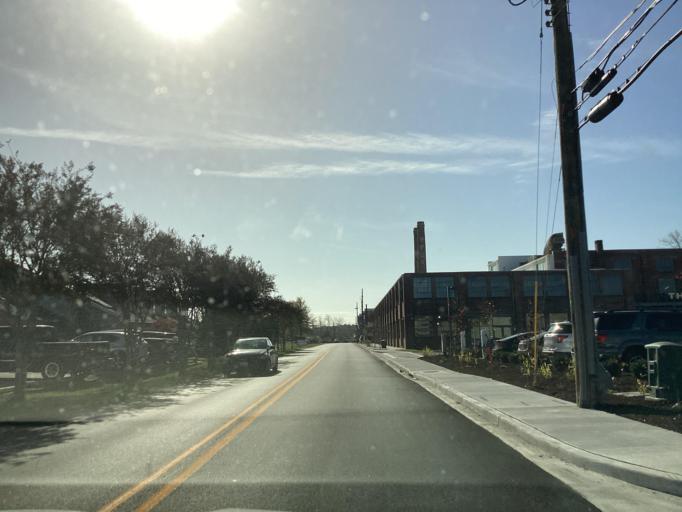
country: US
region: Maryland
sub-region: Dorchester County
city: Cambridge
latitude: 38.5630
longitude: -76.0676
